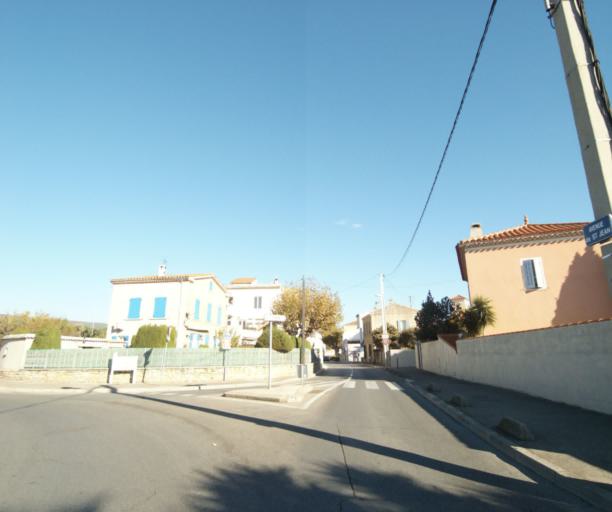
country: FR
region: Provence-Alpes-Cote d'Azur
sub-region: Departement des Bouches-du-Rhone
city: Ceyreste
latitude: 43.1888
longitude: 5.6279
